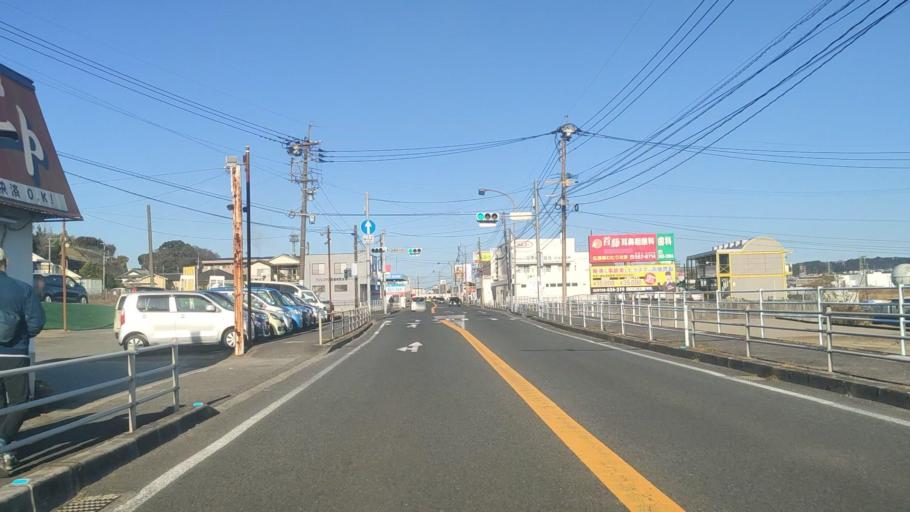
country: JP
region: Oita
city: Oita
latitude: 33.2189
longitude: 131.6151
